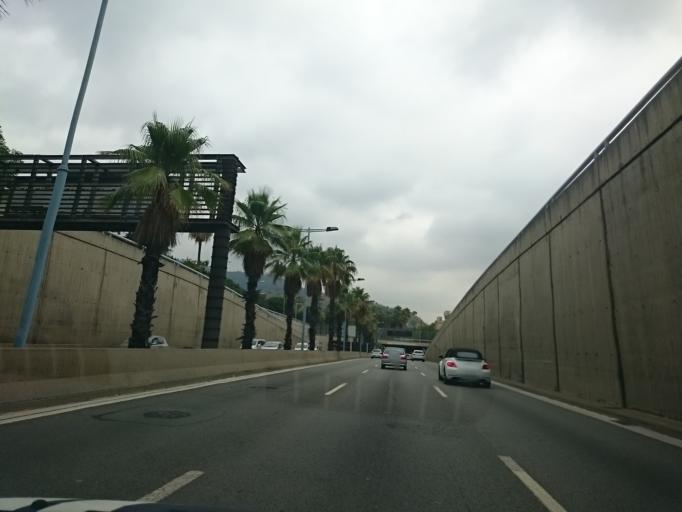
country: ES
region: Catalonia
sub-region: Provincia de Barcelona
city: les Corts
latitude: 41.4016
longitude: 2.1145
